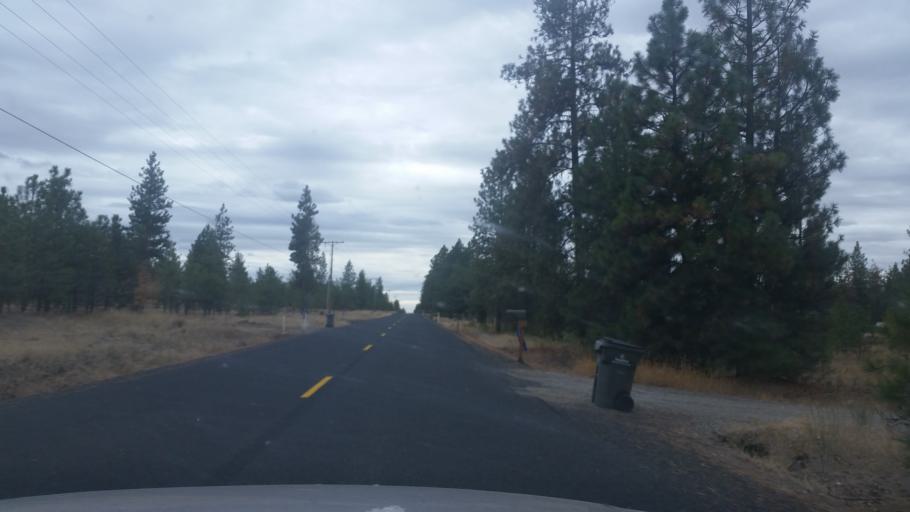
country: US
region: Washington
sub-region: Spokane County
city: Medical Lake
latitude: 47.4704
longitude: -117.7792
